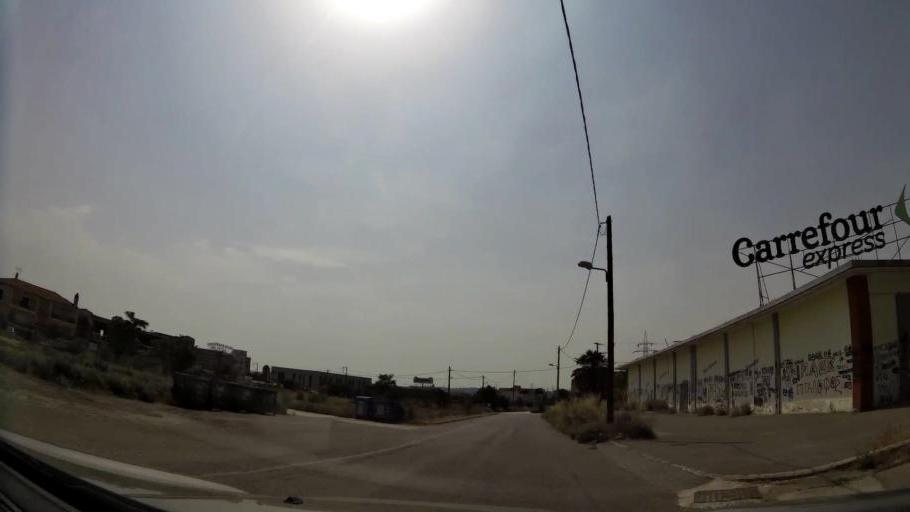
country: GR
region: Central Macedonia
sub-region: Nomos Thessalonikis
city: Efkarpia
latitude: 40.6886
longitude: 22.9480
